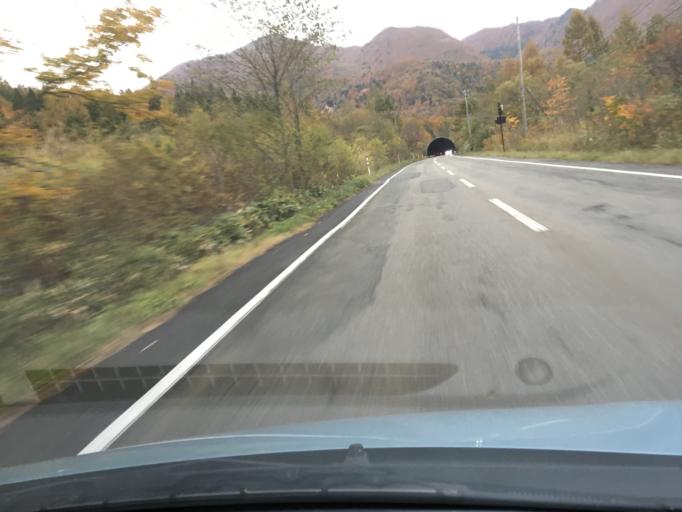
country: JP
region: Iwate
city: Ichinoseki
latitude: 39.0141
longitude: 140.8703
